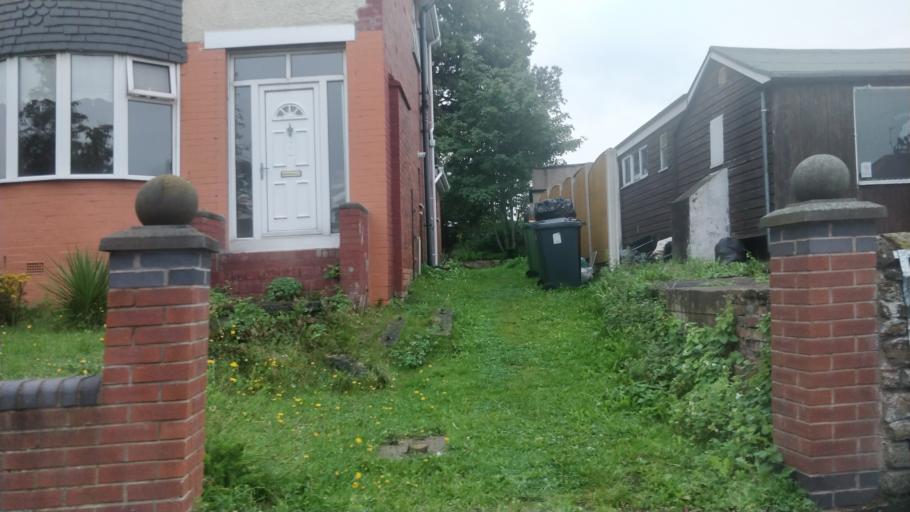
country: GB
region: England
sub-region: Sefton
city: Maghull
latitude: 53.5168
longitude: -2.9456
